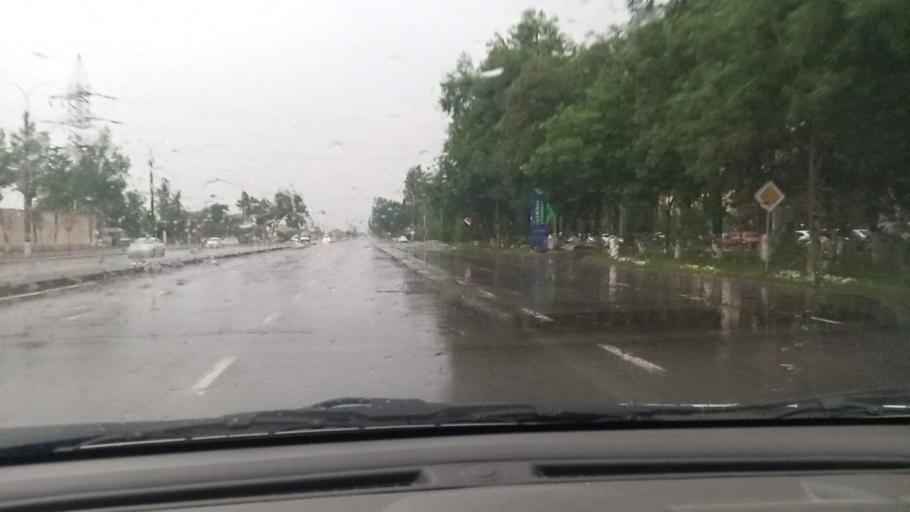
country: UZ
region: Toshkent
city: Salor
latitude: 41.3218
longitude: 69.3629
